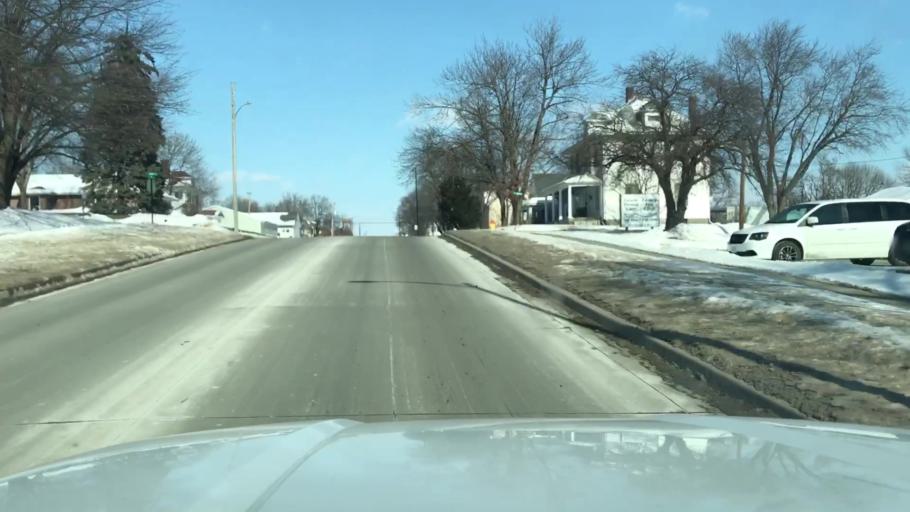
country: US
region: Missouri
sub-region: Nodaway County
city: Maryville
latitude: 40.3417
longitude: -94.8730
